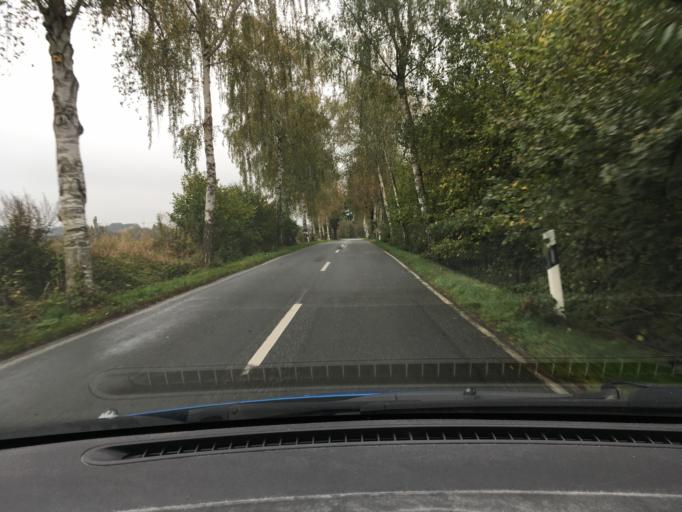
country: DE
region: Schleswig-Holstein
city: Bosau
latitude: 54.0934
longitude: 10.4682
